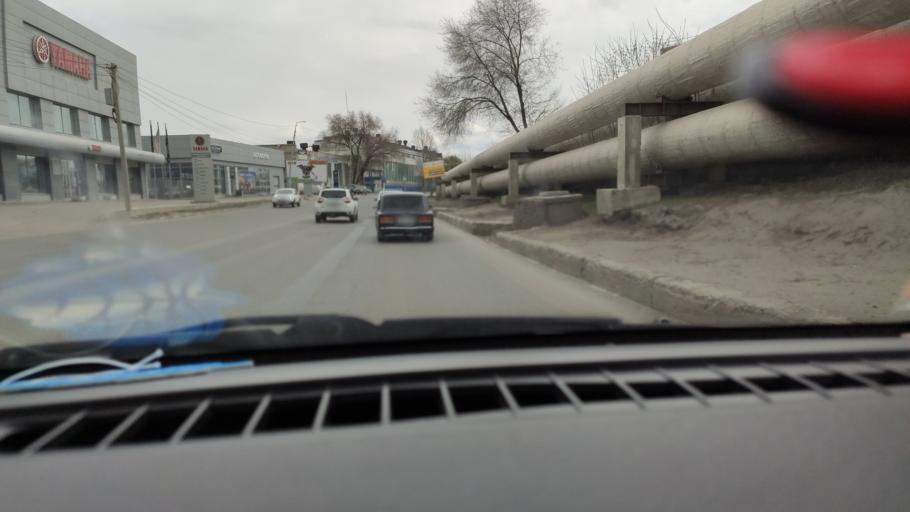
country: RU
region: Saratov
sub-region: Saratovskiy Rayon
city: Saratov
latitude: 51.5638
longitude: 46.0030
